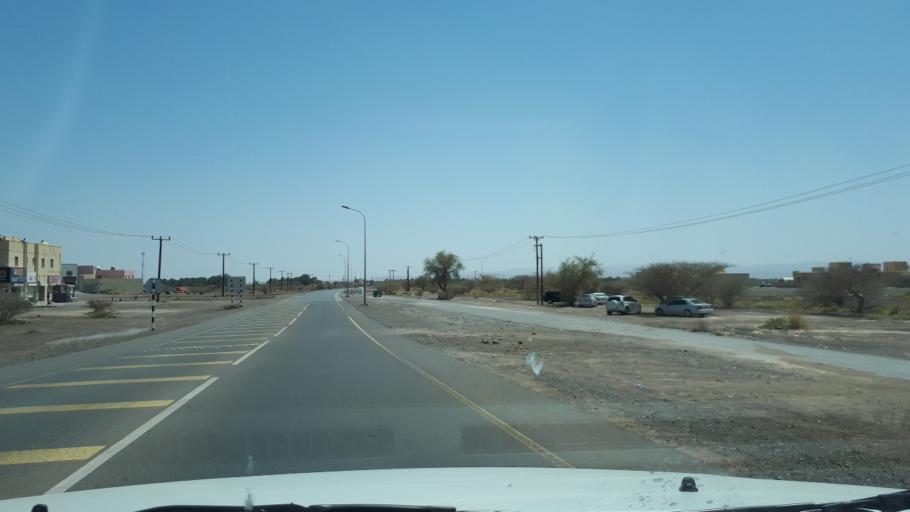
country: OM
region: Muhafazat ad Dakhiliyah
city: Bahla'
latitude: 22.9240
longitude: 57.2557
